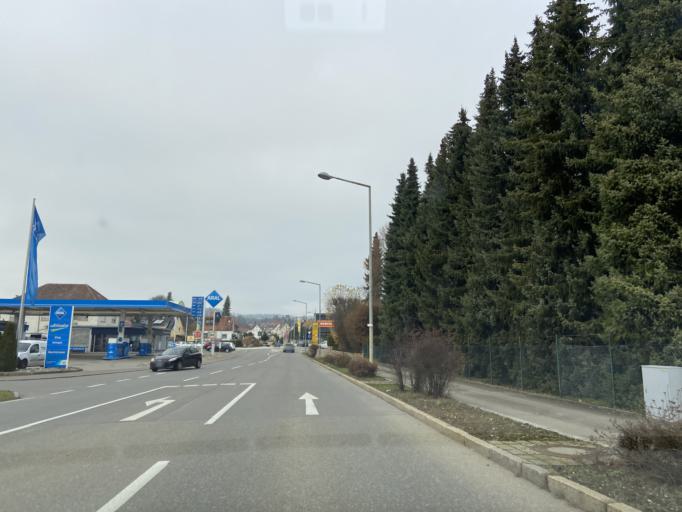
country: DE
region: Baden-Wuerttemberg
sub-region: Tuebingen Region
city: Gammertingen
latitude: 48.2455
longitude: 9.2238
